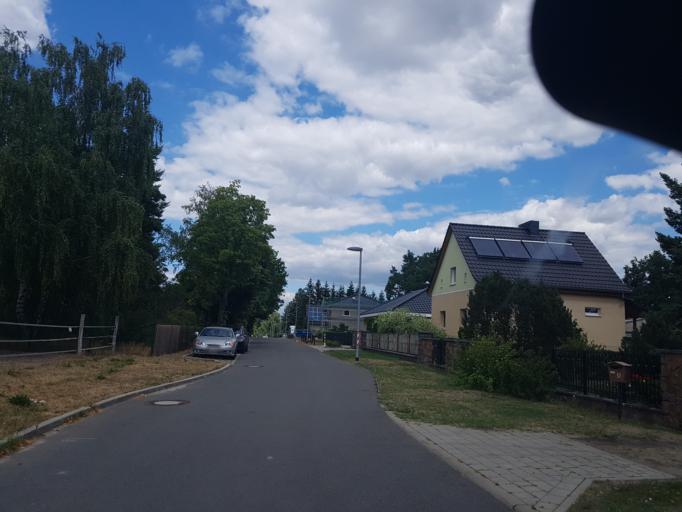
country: DE
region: Brandenburg
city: Teltow
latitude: 52.3695
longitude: 13.2550
